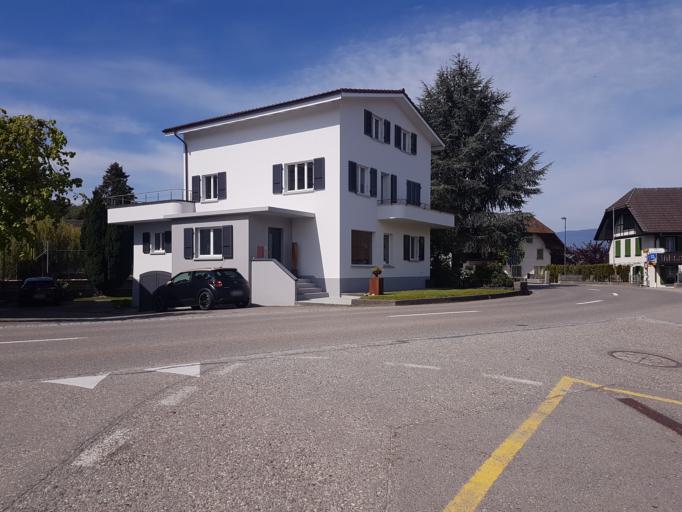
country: CH
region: Bern
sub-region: Seeland District
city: Tauffelen
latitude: 47.0468
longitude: 7.1518
